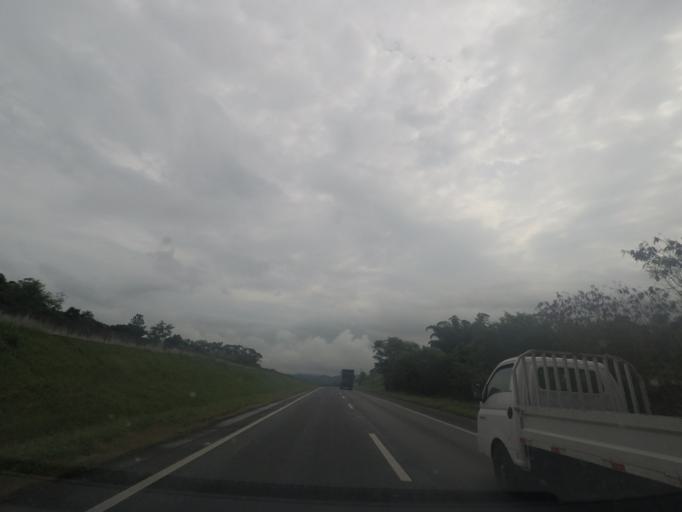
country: BR
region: Sao Paulo
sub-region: Cajati
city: Cajati
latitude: -24.7446
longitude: -48.1447
